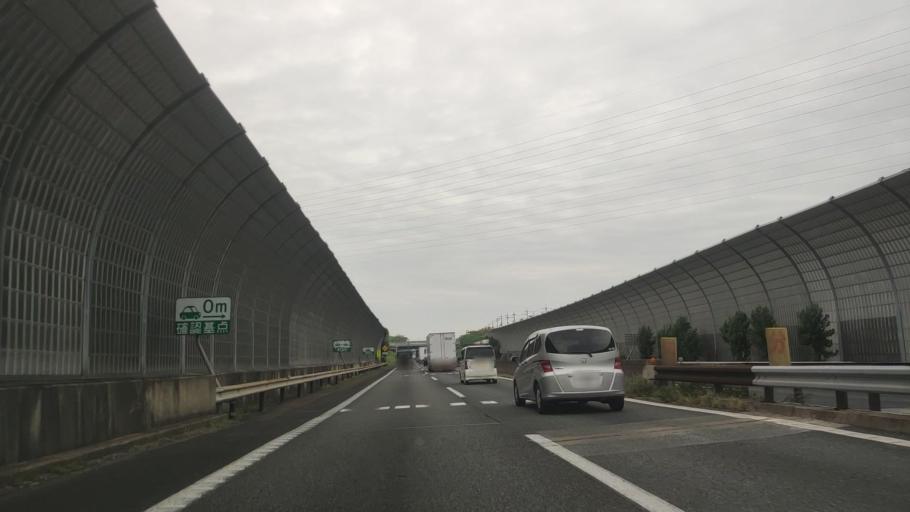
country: JP
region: Nara
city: Tawaramoto
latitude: 34.5745
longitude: 135.7158
